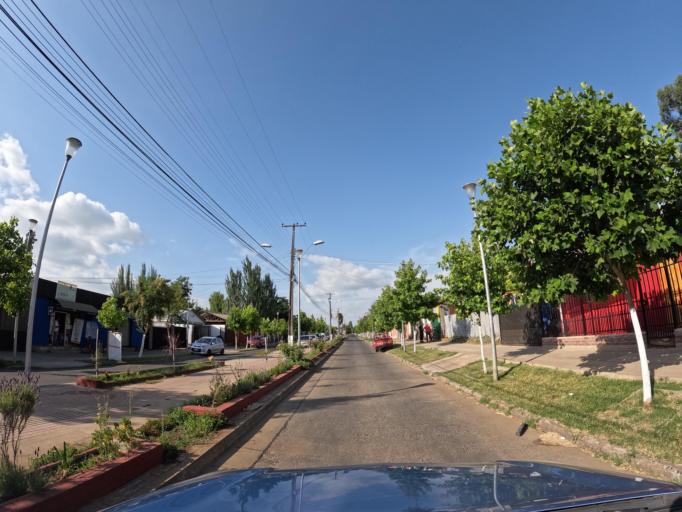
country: CL
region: Maule
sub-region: Provincia de Curico
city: Molina
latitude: -35.2864
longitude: -71.2616
